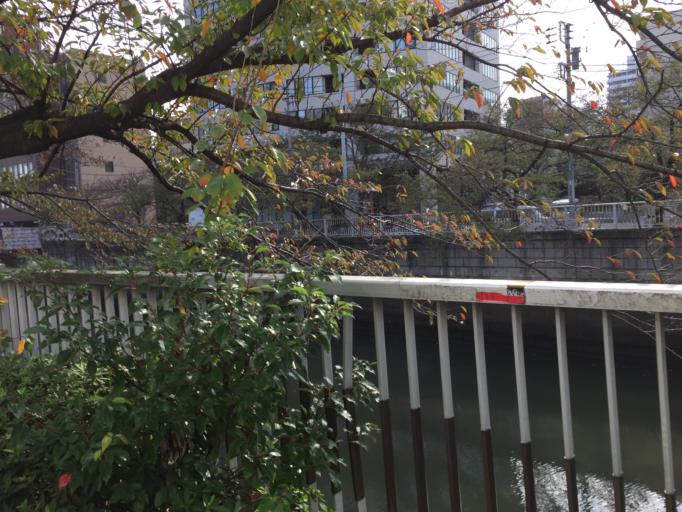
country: JP
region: Tokyo
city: Tokyo
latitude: 35.6329
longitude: 139.7120
